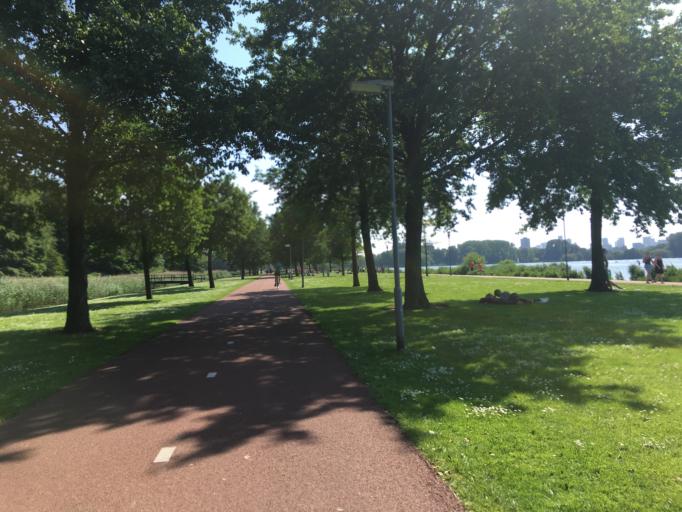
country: NL
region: South Holland
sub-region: Gemeente Rotterdam
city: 's-Gravenland
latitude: 51.9359
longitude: 4.5241
